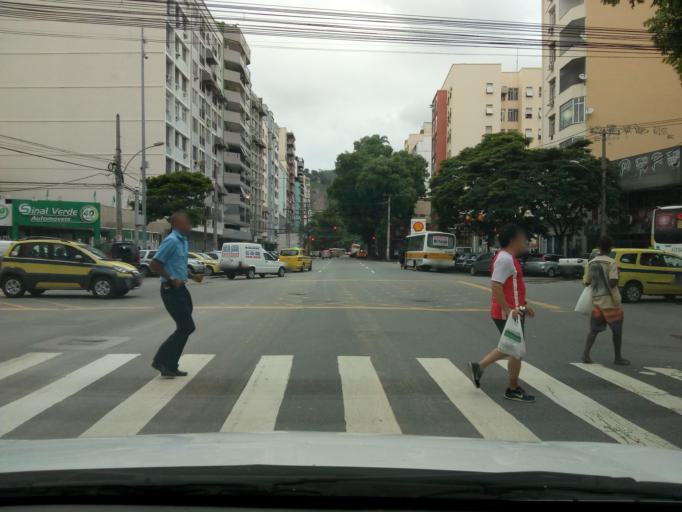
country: BR
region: Rio de Janeiro
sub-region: Rio De Janeiro
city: Rio de Janeiro
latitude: -22.9179
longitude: -43.2245
